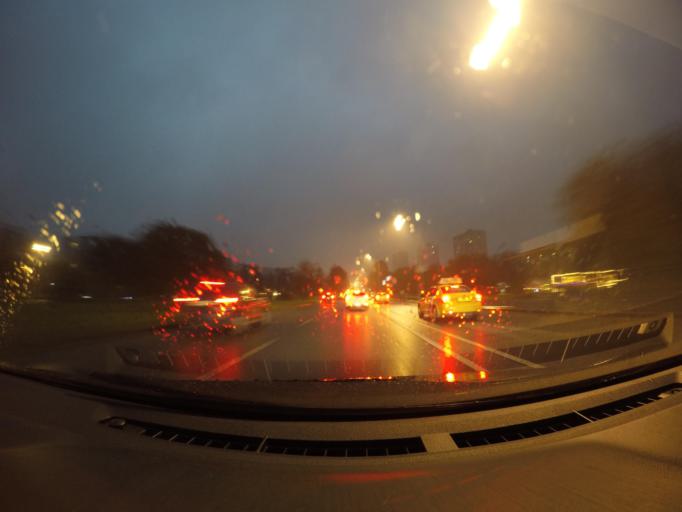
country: RU
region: Moscow
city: Kolomenskoye
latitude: 55.6722
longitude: 37.6630
